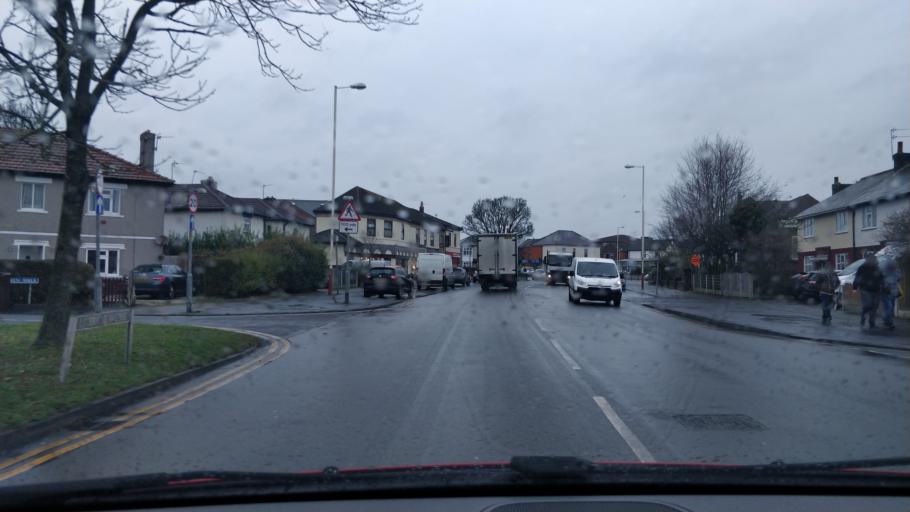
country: GB
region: England
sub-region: Sefton
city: Southport
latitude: 53.6019
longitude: -3.0333
